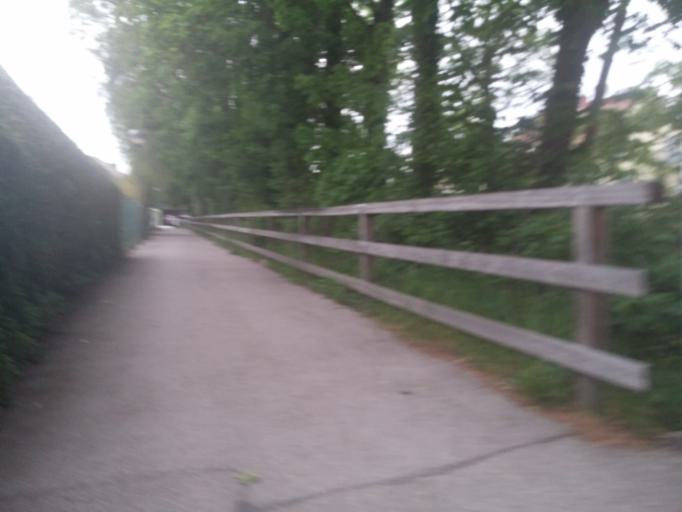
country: DE
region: Bavaria
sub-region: Upper Bavaria
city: Dachau
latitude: 48.2574
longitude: 11.4475
